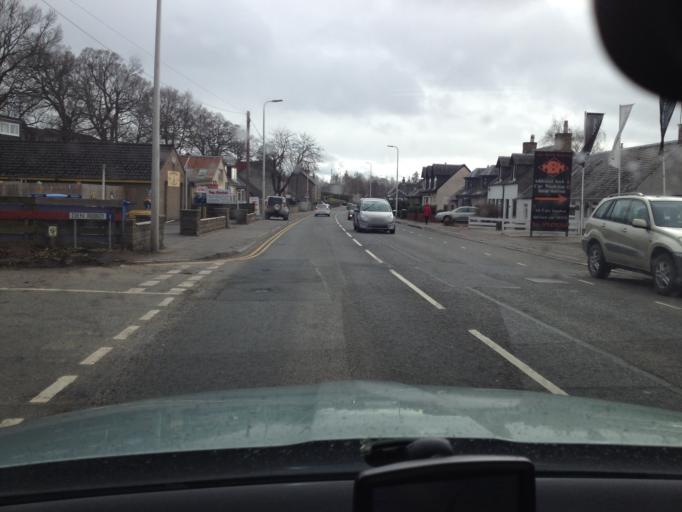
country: GB
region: Scotland
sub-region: Perth and Kinross
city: Scone
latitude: 56.4164
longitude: -3.4037
